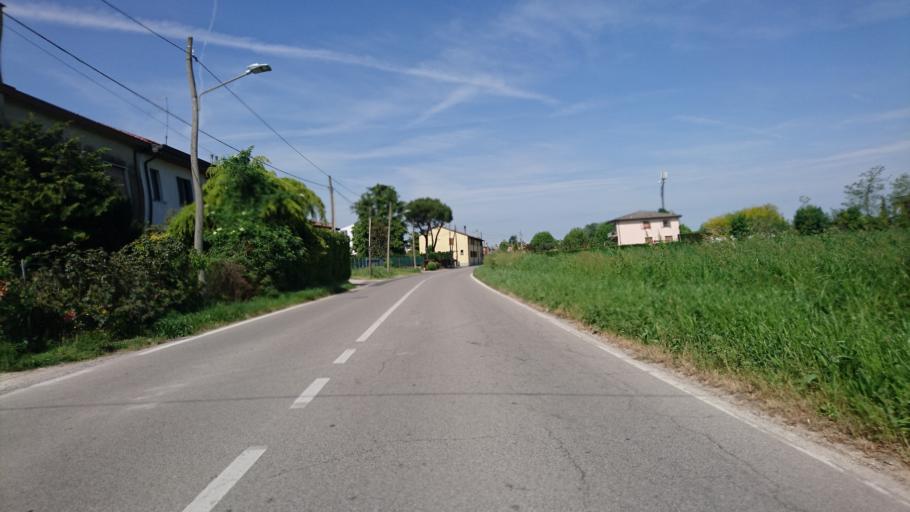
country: IT
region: Veneto
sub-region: Provincia di Padova
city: Vigodarzere
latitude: 45.4480
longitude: 11.8810
